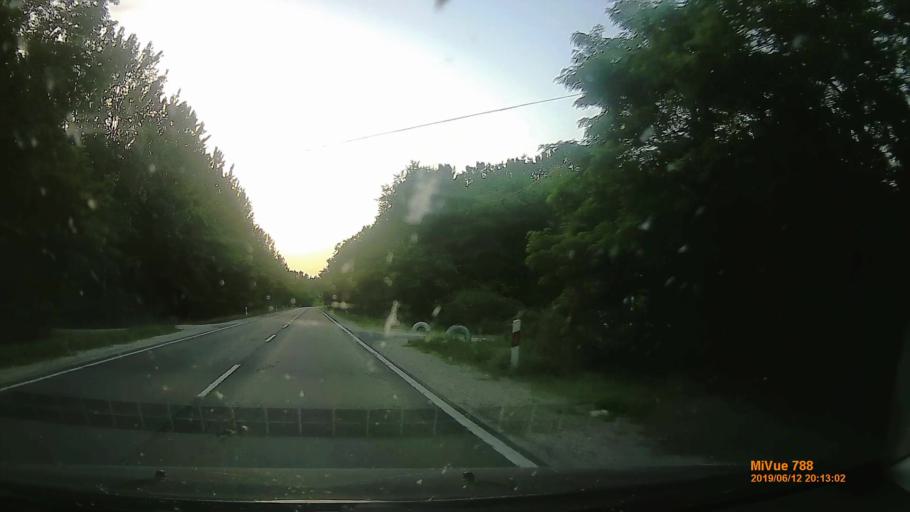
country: HU
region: Pest
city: Alsonemedi
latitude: 47.2940
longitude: 19.1860
